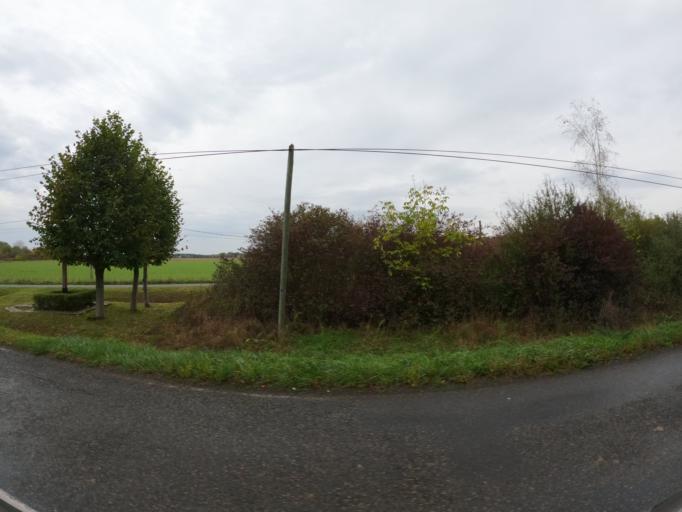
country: FR
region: Ile-de-France
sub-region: Departement de Seine-et-Marne
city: Villeneuve-le-Comte
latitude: 48.8201
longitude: 2.8316
